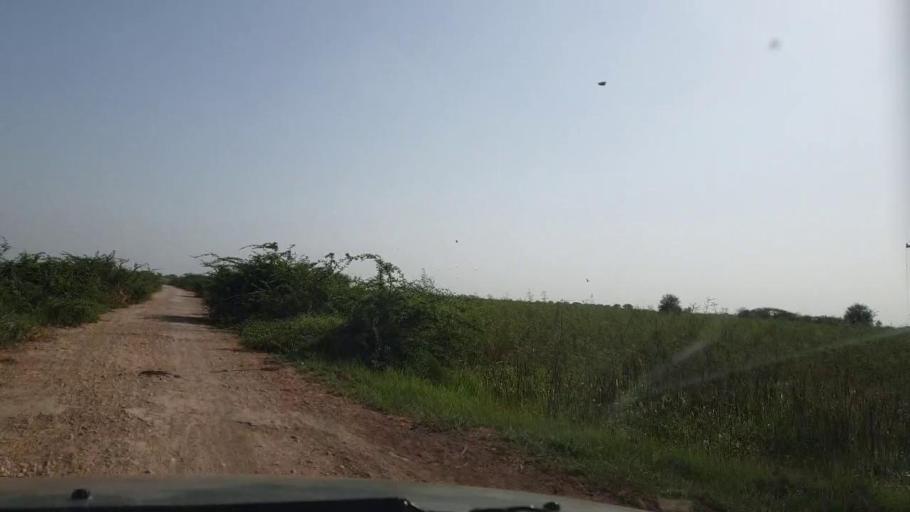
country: PK
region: Sindh
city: Mirwah Gorchani
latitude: 25.2459
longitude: 68.9392
